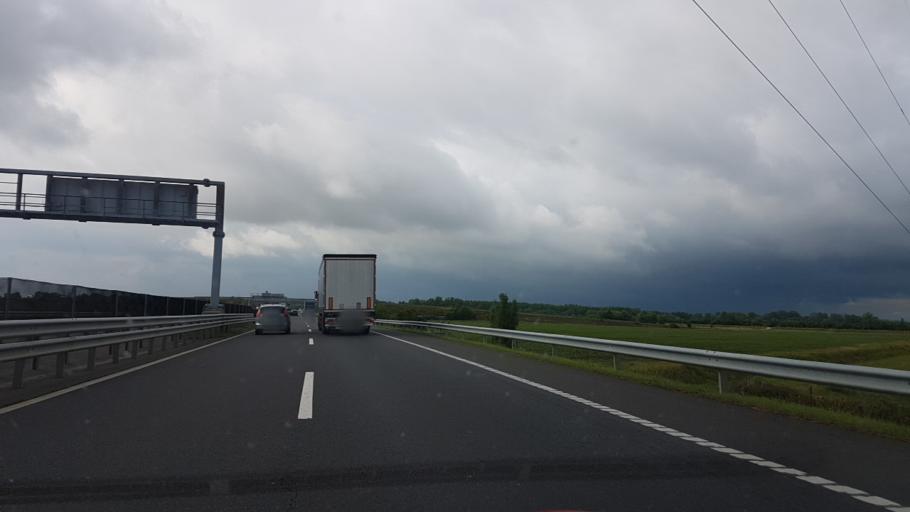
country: HU
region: Borsod-Abauj-Zemplen
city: Alsozsolca
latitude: 48.0718
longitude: 20.8492
